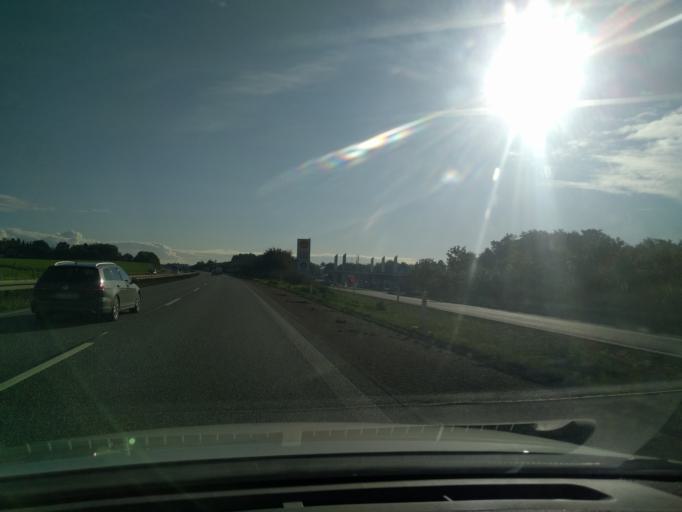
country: DK
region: Zealand
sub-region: Soro Kommune
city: Soro
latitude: 55.4521
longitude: 11.5928
